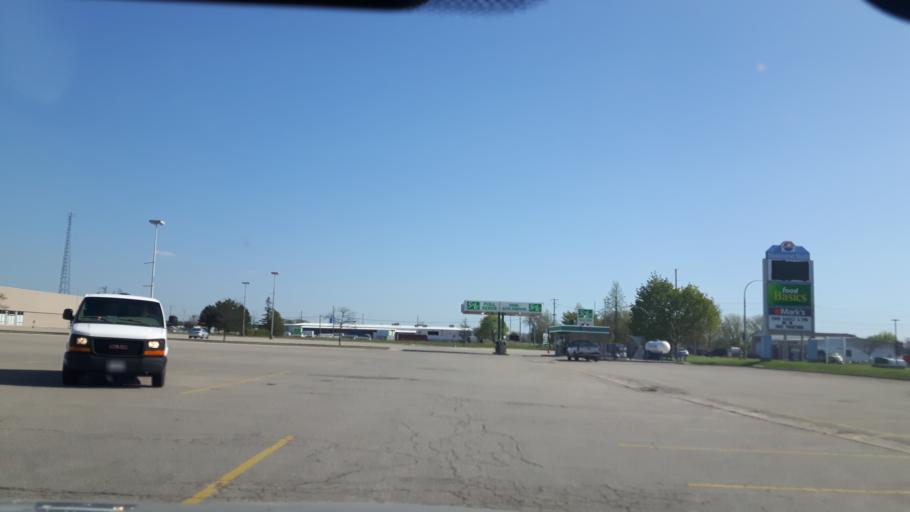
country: CA
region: Ontario
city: Goderich
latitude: 43.7301
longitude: -81.7054
